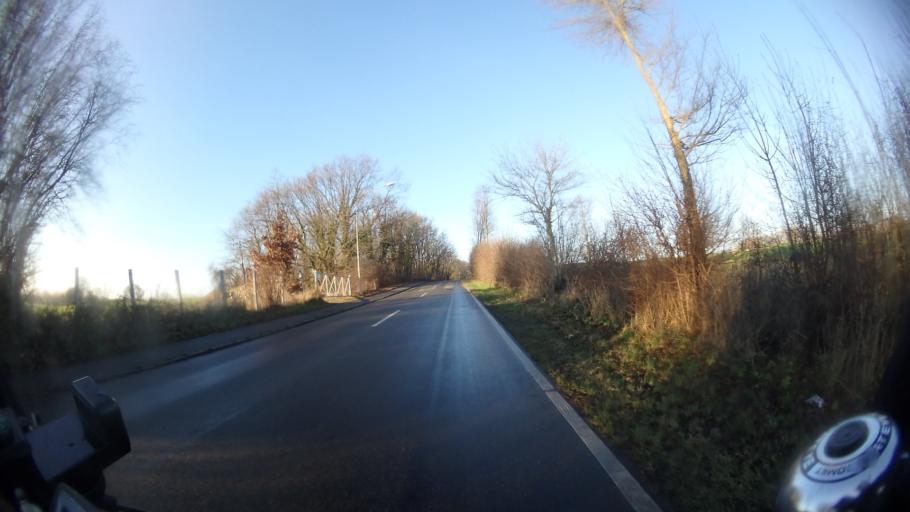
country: DE
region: Schleswig-Holstein
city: Travemuende
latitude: 53.9791
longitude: 10.8650
